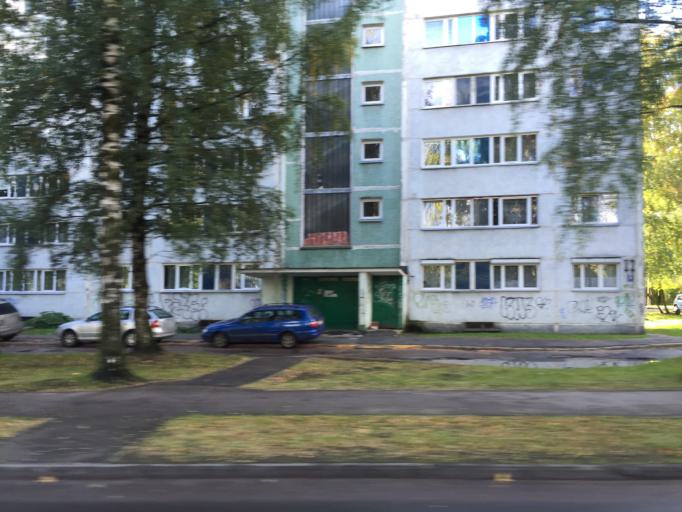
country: LV
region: Marupe
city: Marupe
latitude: 56.9484
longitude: 24.0579
